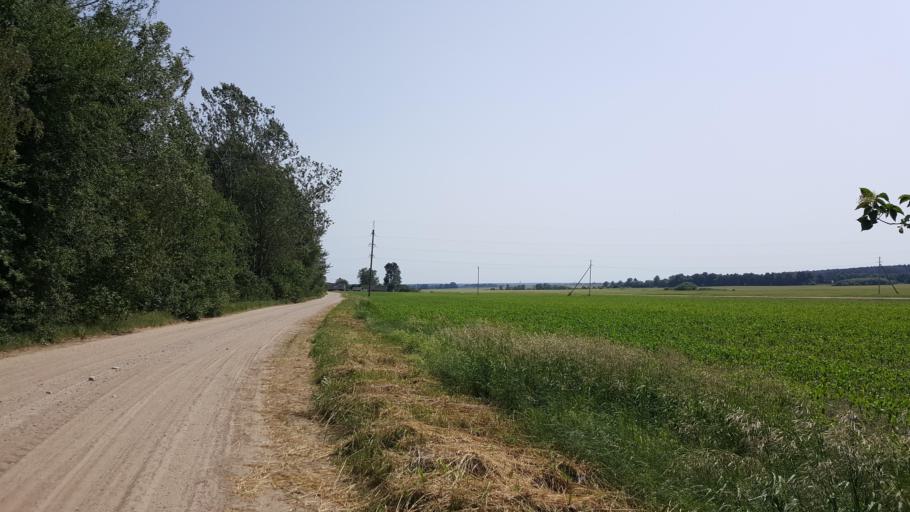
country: BY
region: Brest
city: Kamyanyets
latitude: 52.4655
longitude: 23.8308
